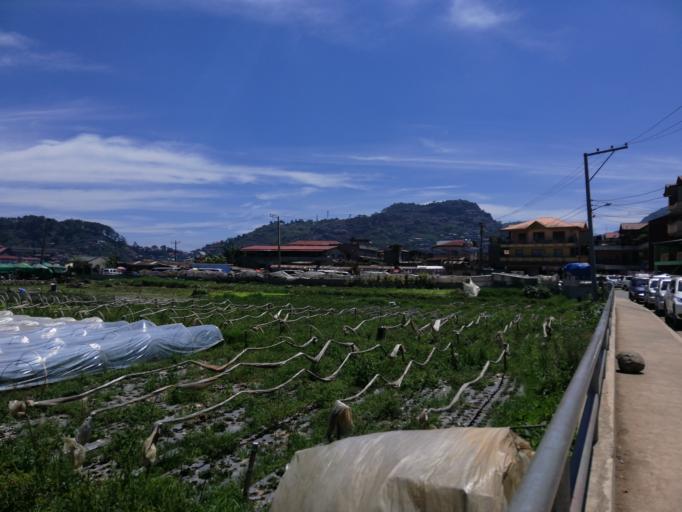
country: PH
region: Cordillera
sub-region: Province of Benguet
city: La Trinidad
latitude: 16.4538
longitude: 120.5843
